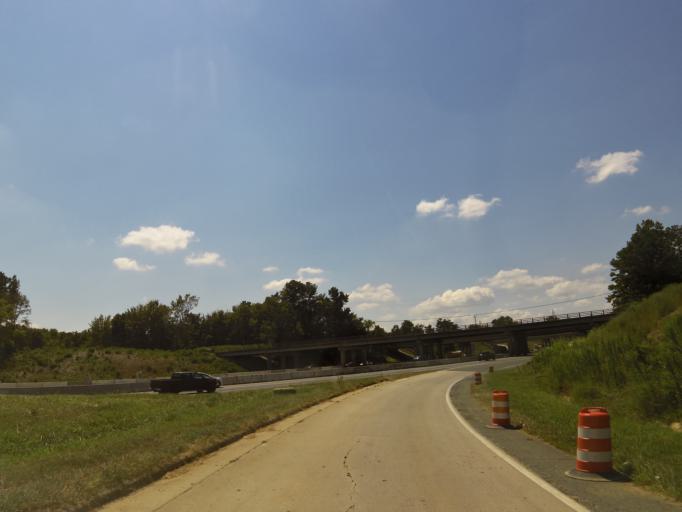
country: US
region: North Carolina
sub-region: Cabarrus County
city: Kannapolis
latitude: 35.4461
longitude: -80.6111
